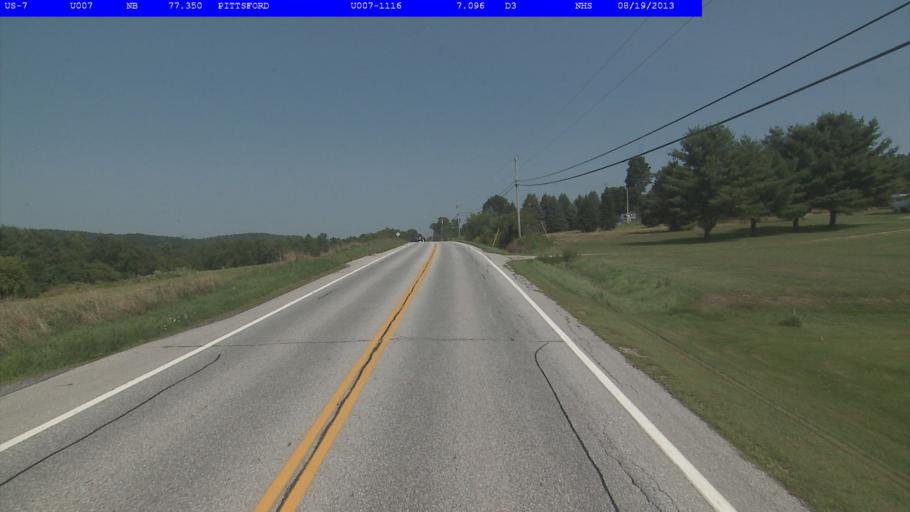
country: US
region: Vermont
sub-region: Rutland County
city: Brandon
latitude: 43.7472
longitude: -73.0472
